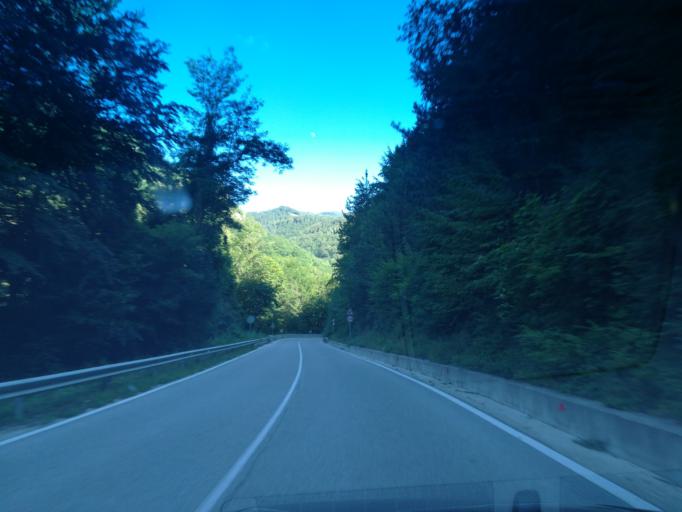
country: BG
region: Smolyan
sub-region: Obshtina Chepelare
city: Chepelare
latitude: 41.8078
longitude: 24.7078
